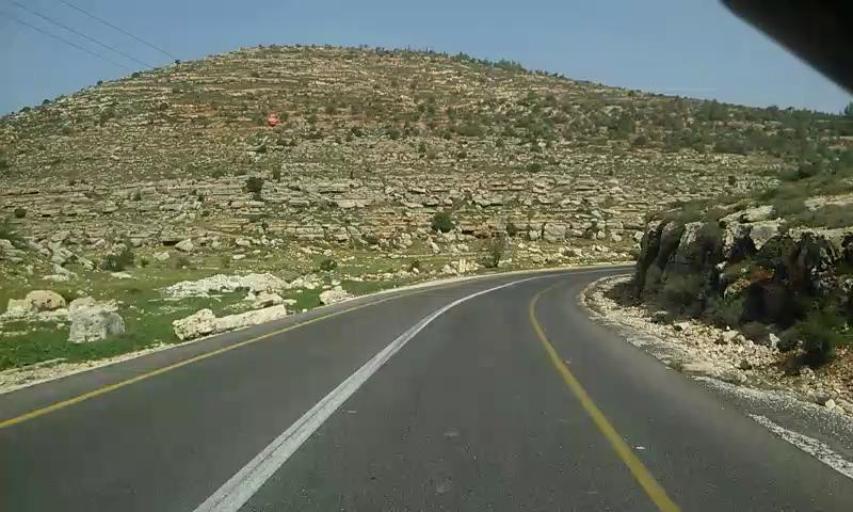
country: PS
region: West Bank
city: `Atarah
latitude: 31.9996
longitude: 35.2240
